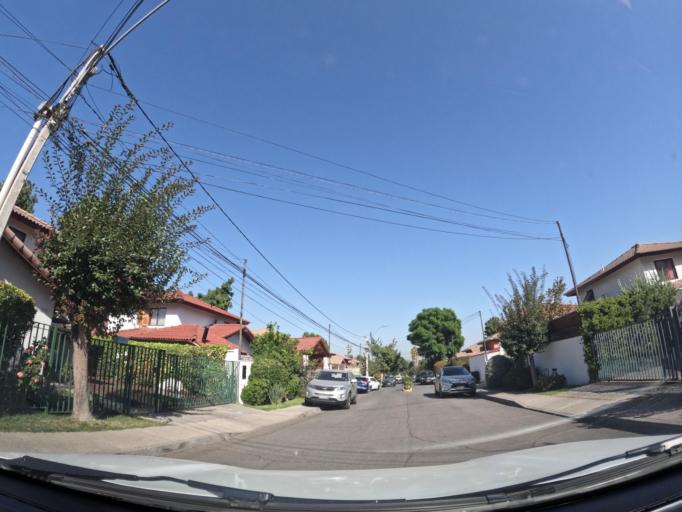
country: CL
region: Santiago Metropolitan
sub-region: Provincia de Santiago
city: Villa Presidente Frei, Nunoa, Santiago, Chile
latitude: -33.5053
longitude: -70.5567
